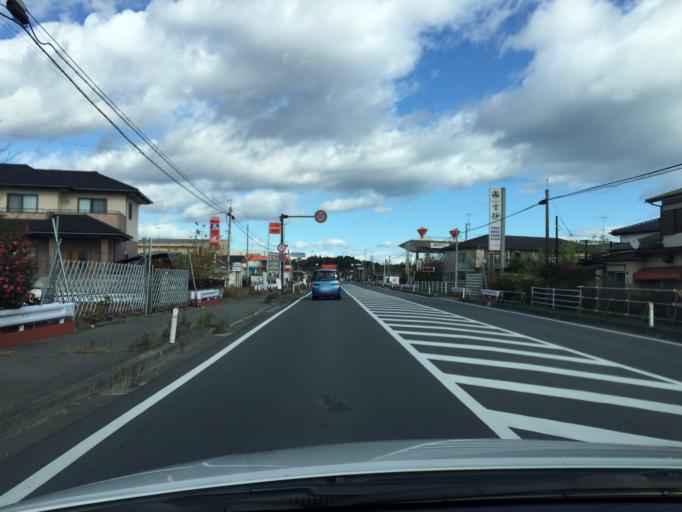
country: JP
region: Fukushima
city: Namie
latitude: 37.4514
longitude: 141.0092
